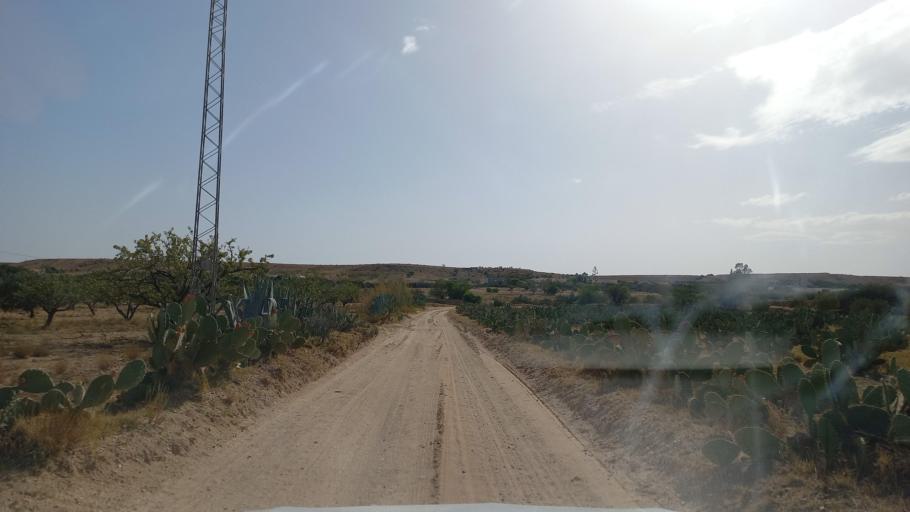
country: TN
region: Al Qasrayn
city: Kasserine
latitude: 35.2639
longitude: 8.9316
